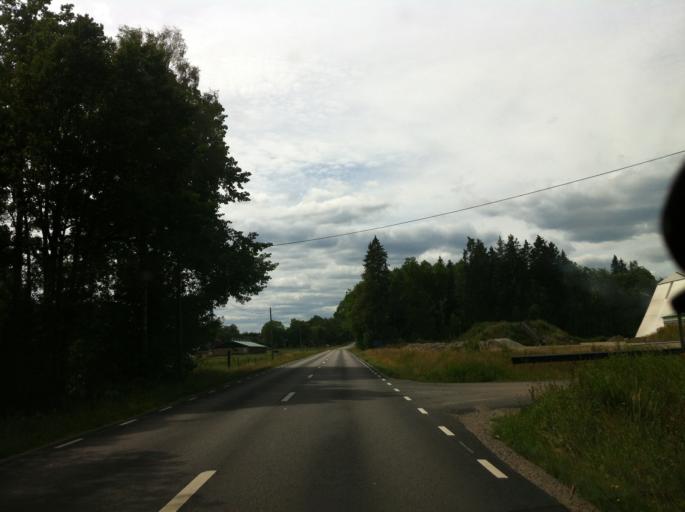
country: SE
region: Kronoberg
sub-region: Lessebo Kommun
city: Lessebo
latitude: 56.5521
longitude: 15.2407
